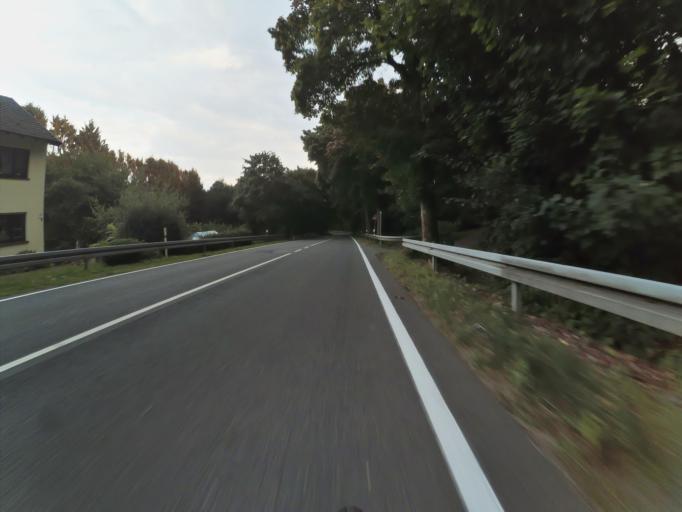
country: DE
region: North Rhine-Westphalia
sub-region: Regierungsbezirk Munster
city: Tecklenburg
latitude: 52.2750
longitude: 7.8270
